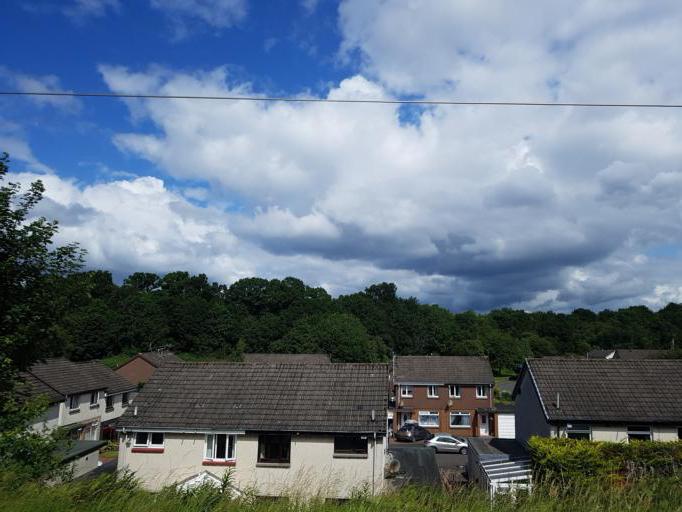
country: GB
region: Scotland
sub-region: Falkirk
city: Polmont
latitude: 55.9836
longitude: -3.7031
